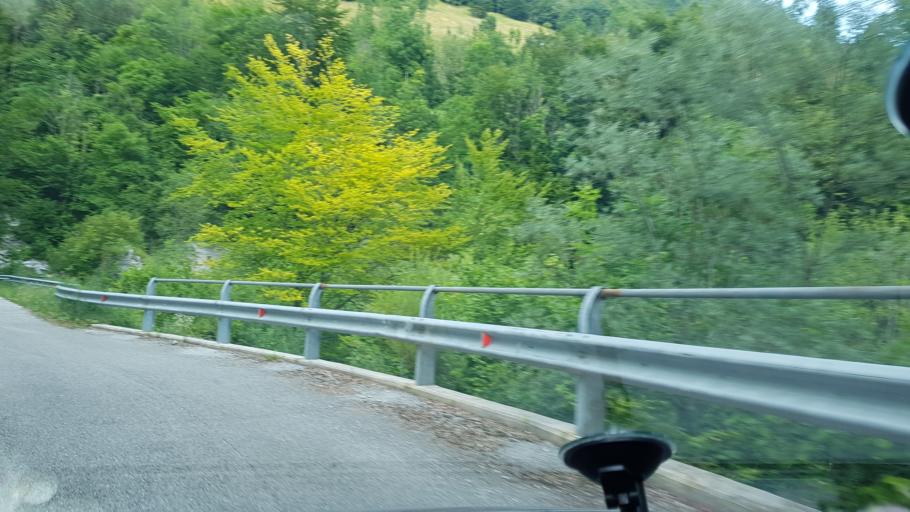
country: IT
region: Friuli Venezia Giulia
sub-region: Provincia di Udine
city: Taipana
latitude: 46.3145
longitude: 13.3925
